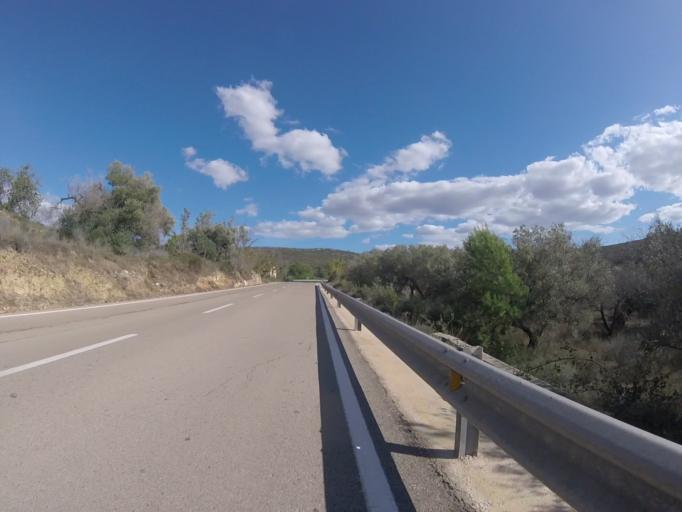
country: ES
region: Valencia
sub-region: Provincia de Castello
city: Cuevas de Vinroma
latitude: 40.2953
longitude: 0.1760
